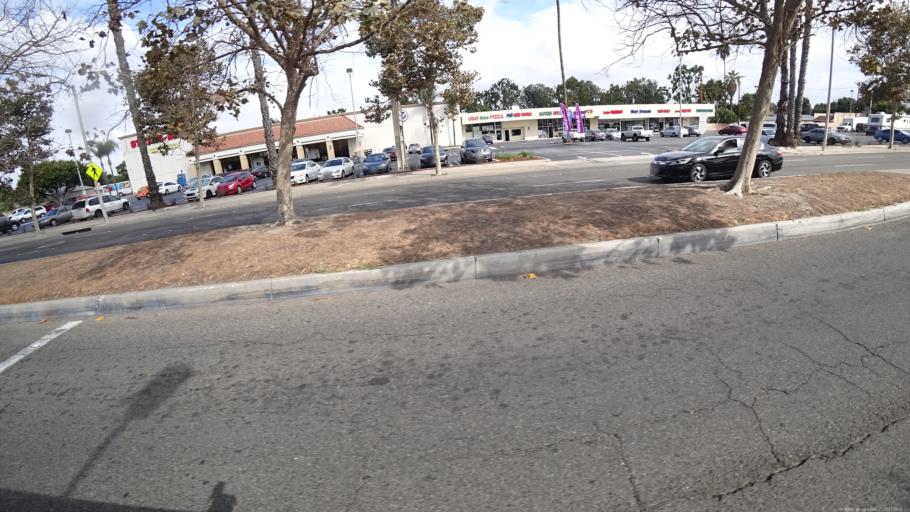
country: US
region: California
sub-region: Orange County
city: Santa Ana
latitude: 33.7598
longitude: -117.9044
